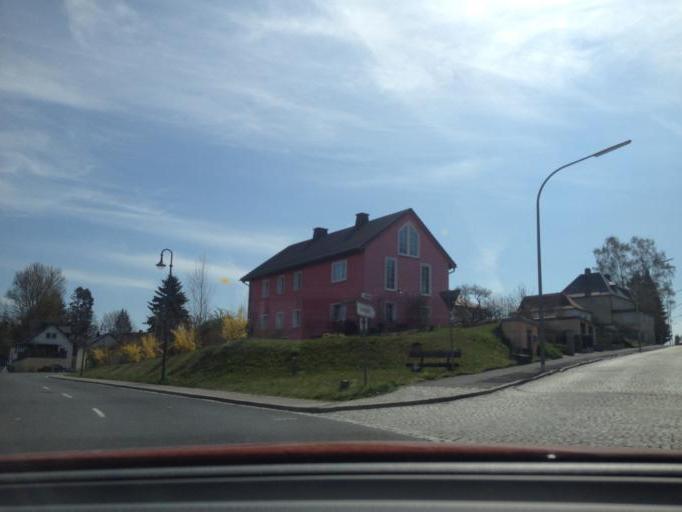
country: DE
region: Bavaria
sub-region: Upper Franconia
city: Roslau
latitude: 50.0815
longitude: 11.9782
